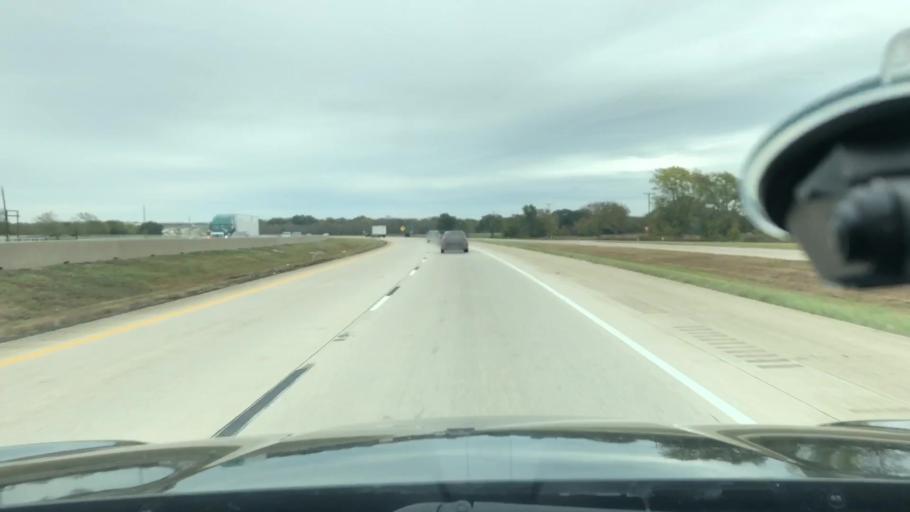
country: US
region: Texas
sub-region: Hopkins County
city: Sulphur Springs
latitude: 33.1196
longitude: -95.7233
